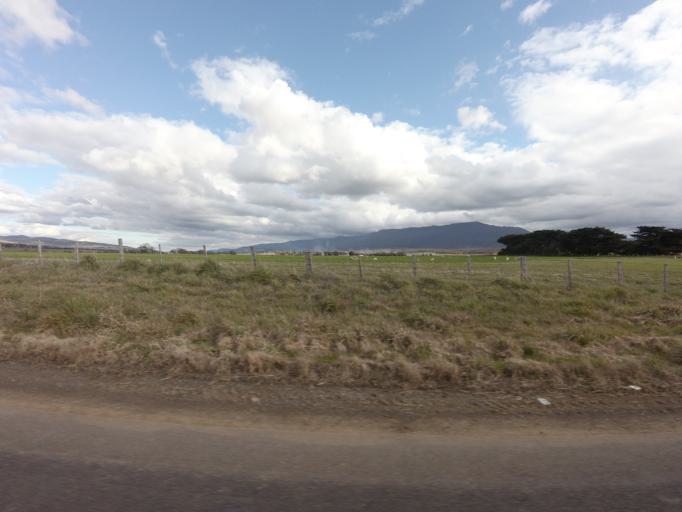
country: AU
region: Tasmania
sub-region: Northern Midlands
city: Longford
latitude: -41.8571
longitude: 147.2347
